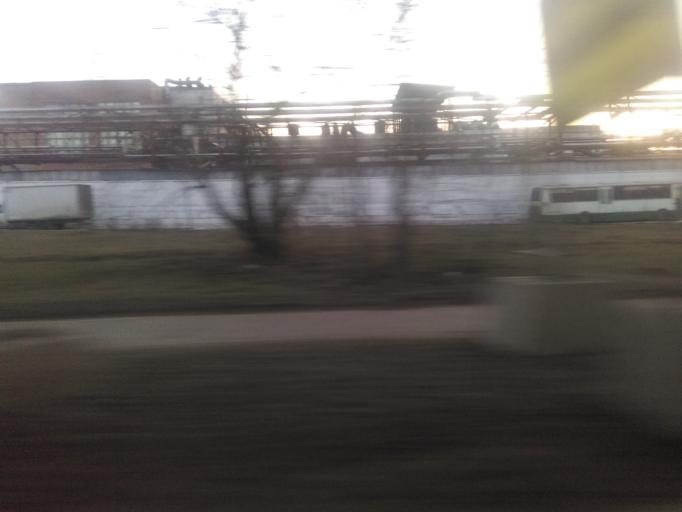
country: RU
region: Moscow
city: Mikhalkovo
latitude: 55.6774
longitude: 37.4346
